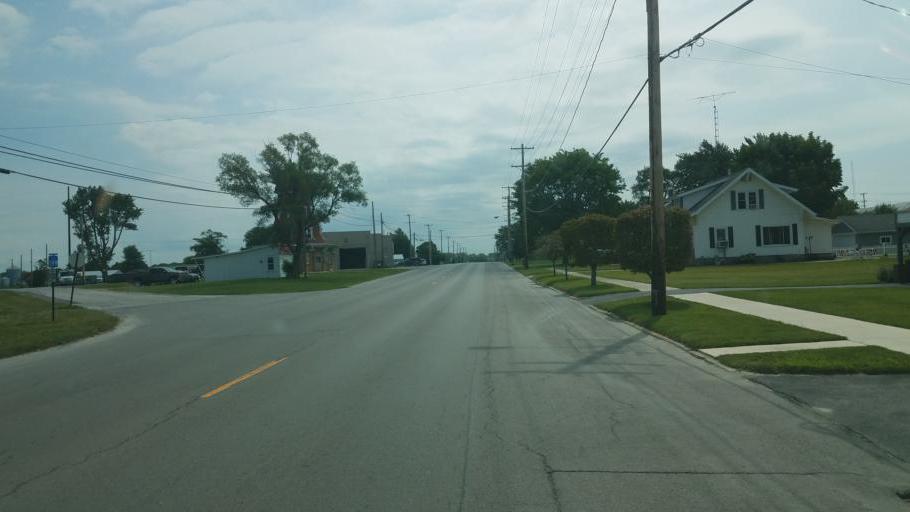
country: US
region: Ohio
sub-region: Wyandot County
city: Carey
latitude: 40.9502
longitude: -83.3694
